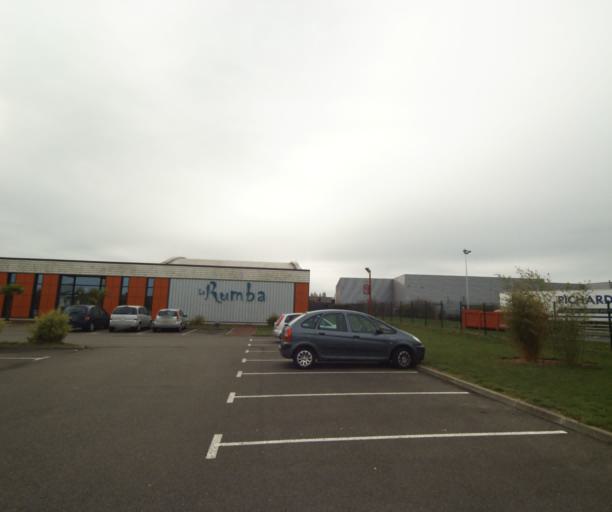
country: FR
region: Centre
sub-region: Departement d'Eure-et-Loir
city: Dreux
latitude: 48.7524
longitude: 1.3522
